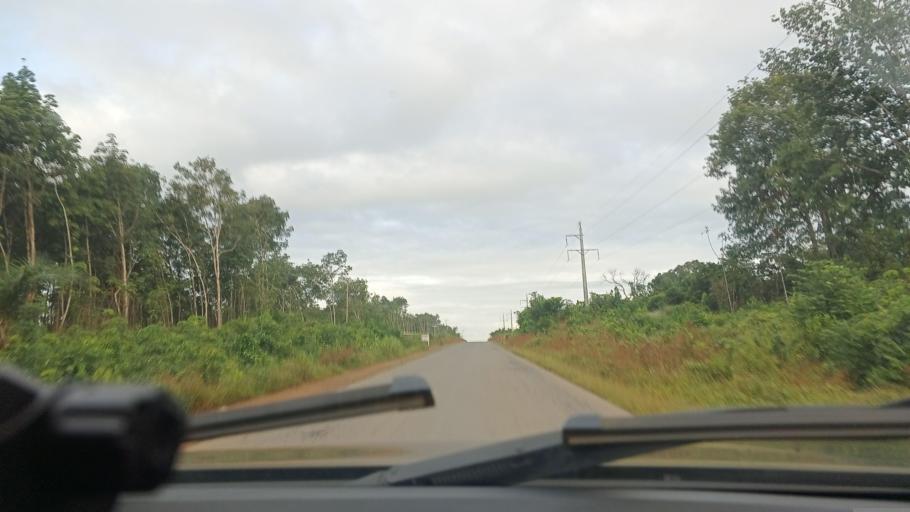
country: LR
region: Montserrado
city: Monrovia
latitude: 6.5429
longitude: -10.8582
